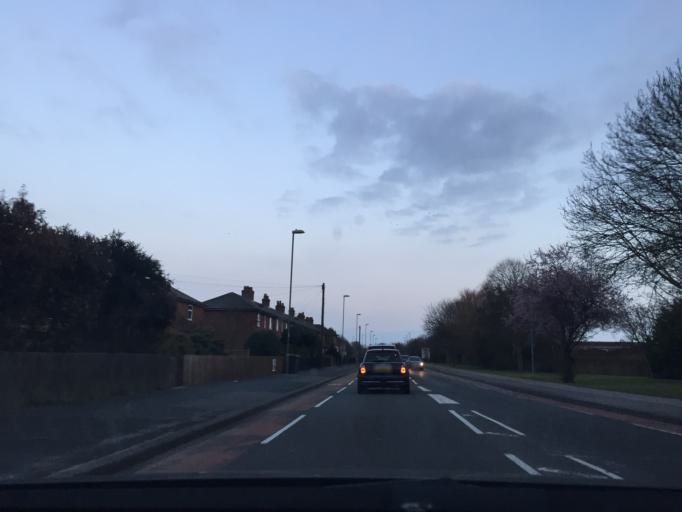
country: GB
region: England
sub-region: Hampshire
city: Fareham
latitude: 50.8201
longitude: -1.1625
